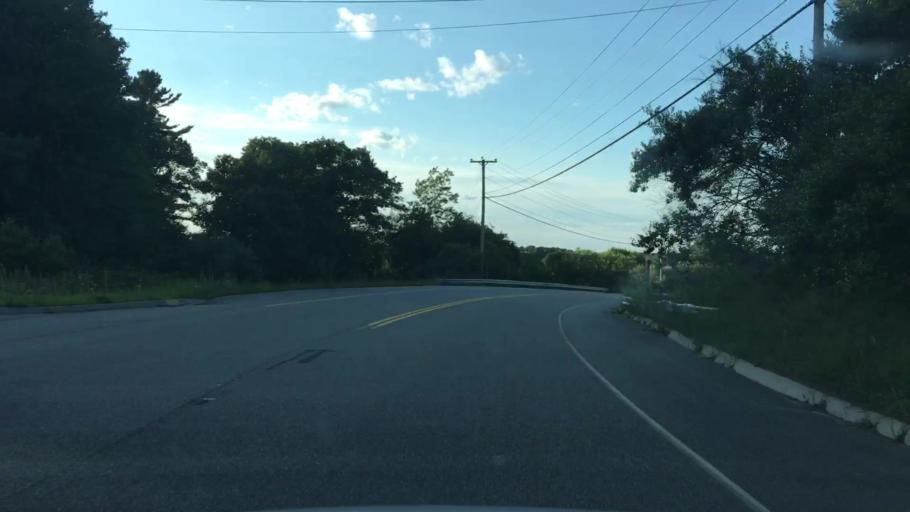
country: US
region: Maine
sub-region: Cumberland County
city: Scarborough
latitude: 43.5938
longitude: -70.2981
